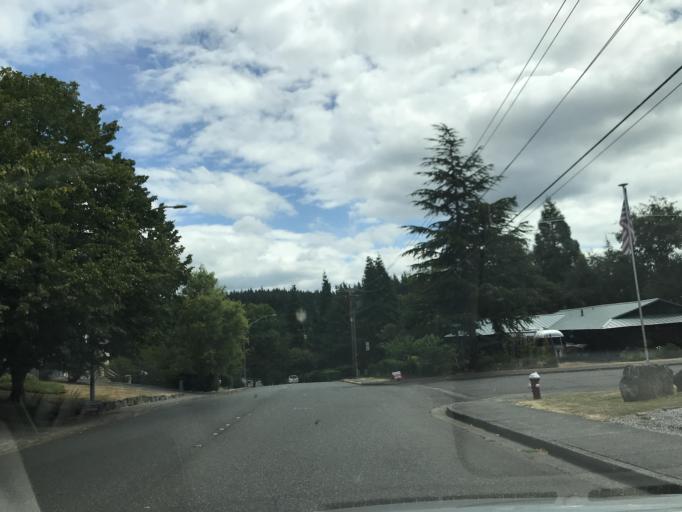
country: US
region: Washington
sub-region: Whatcom County
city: Bellingham
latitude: 48.7101
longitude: -122.5037
